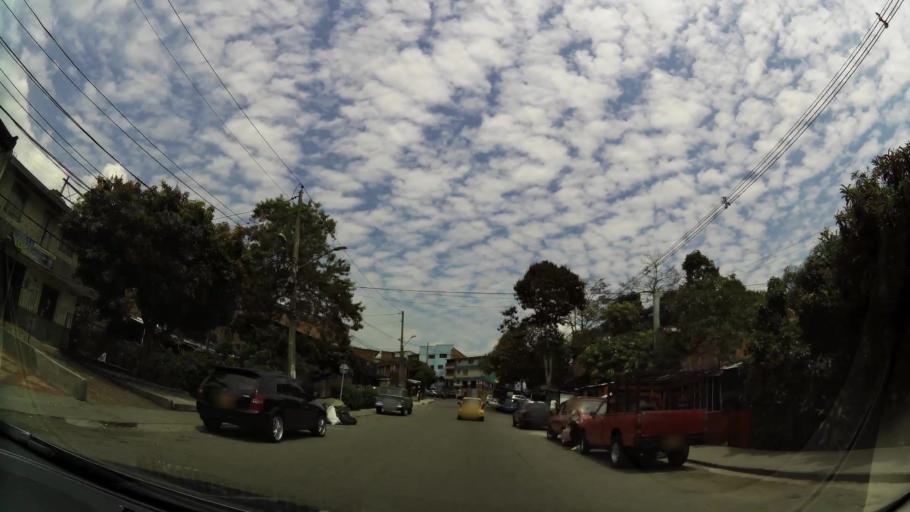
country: CO
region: Antioquia
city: Bello
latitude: 6.3073
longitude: -75.5767
